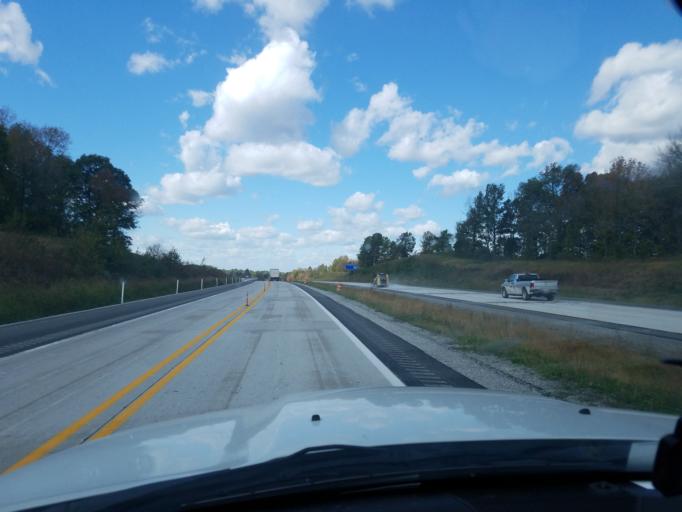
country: US
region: Kentucky
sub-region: Ohio County
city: Beaver Dam
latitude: 37.4439
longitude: -86.8625
